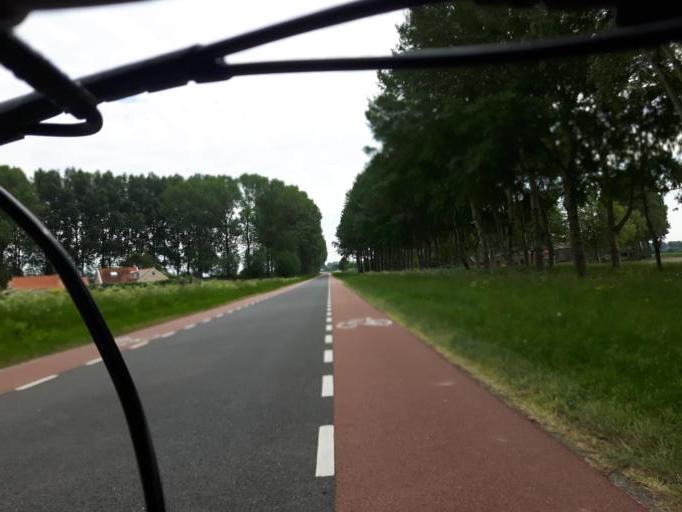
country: NL
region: Zeeland
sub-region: Gemeente Borsele
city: Borssele
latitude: 51.4411
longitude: 3.7779
